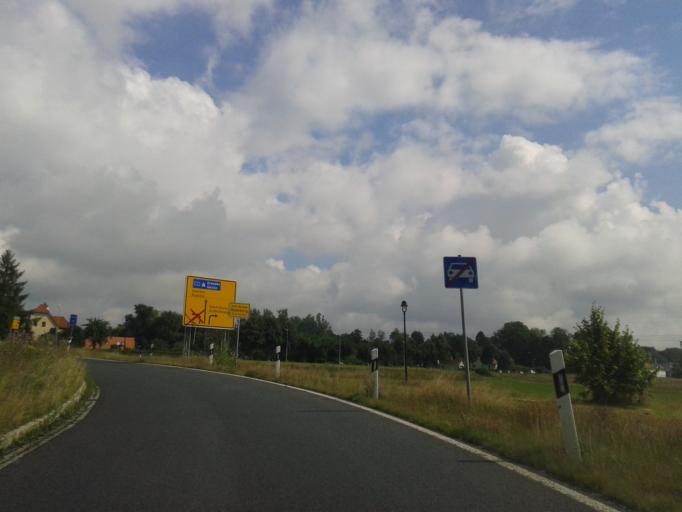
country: DE
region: Saxony
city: Radeberg
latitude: 51.1239
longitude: 13.9372
